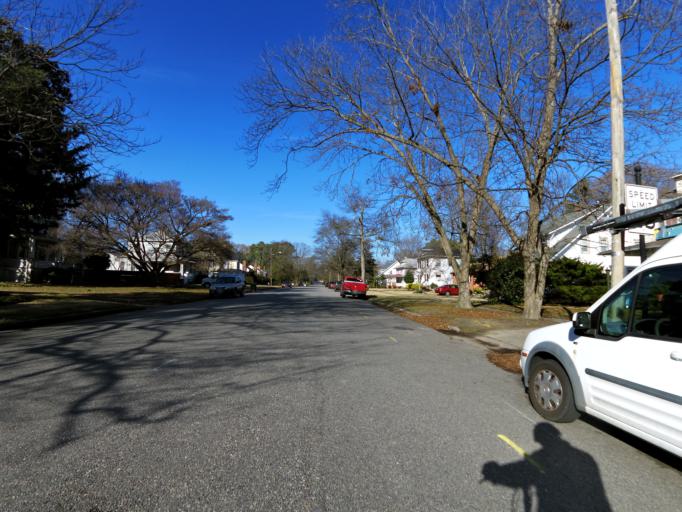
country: US
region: Virginia
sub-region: City of Hampton
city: Hampton
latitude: 37.0011
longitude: -76.3691
